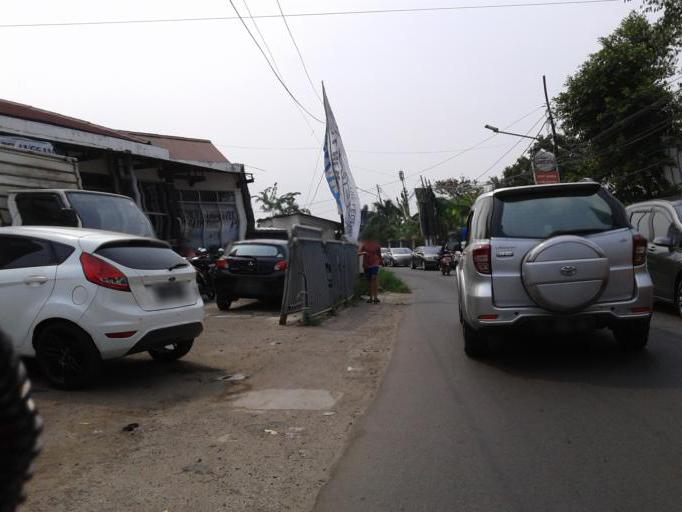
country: ID
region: Banten
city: South Tangerang
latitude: -6.2948
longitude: 106.7343
